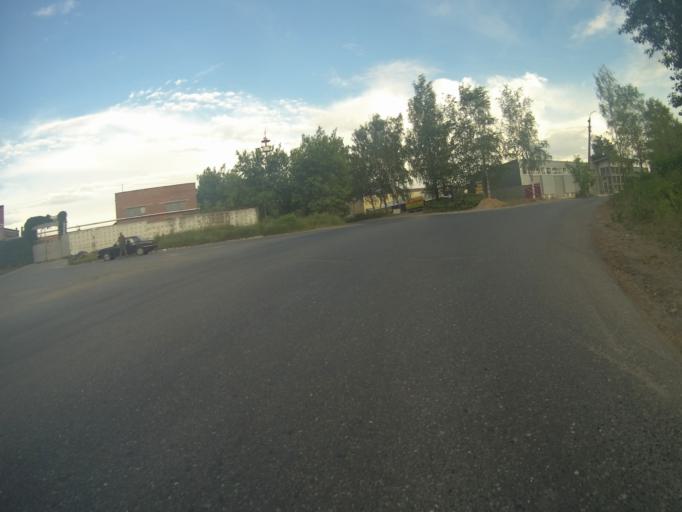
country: RU
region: Vladimir
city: Vladimir
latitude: 56.1616
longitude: 40.3801
